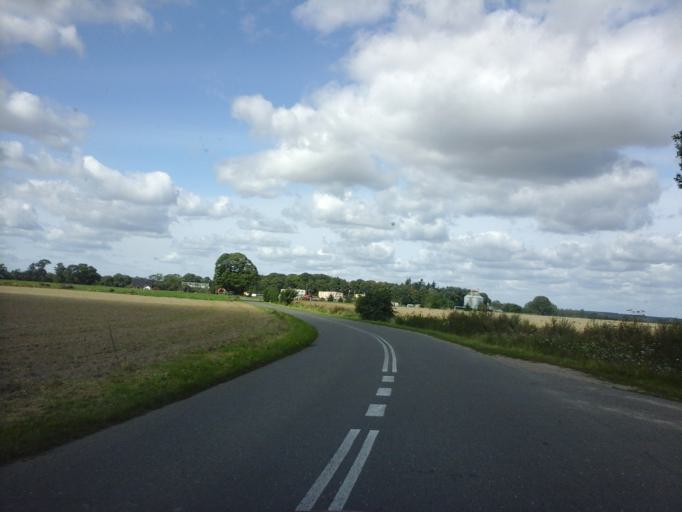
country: PL
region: West Pomeranian Voivodeship
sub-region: Powiat pyrzycki
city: Warnice
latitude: 53.3142
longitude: 14.9522
